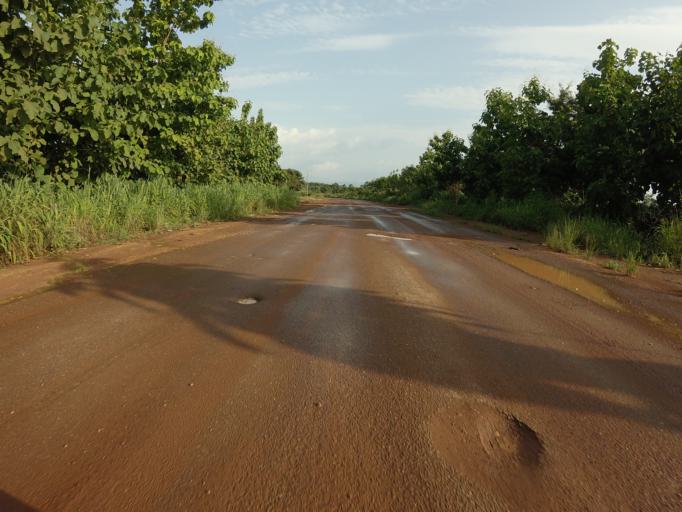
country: GH
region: Volta
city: Kpandu
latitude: 7.0128
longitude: 0.4283
